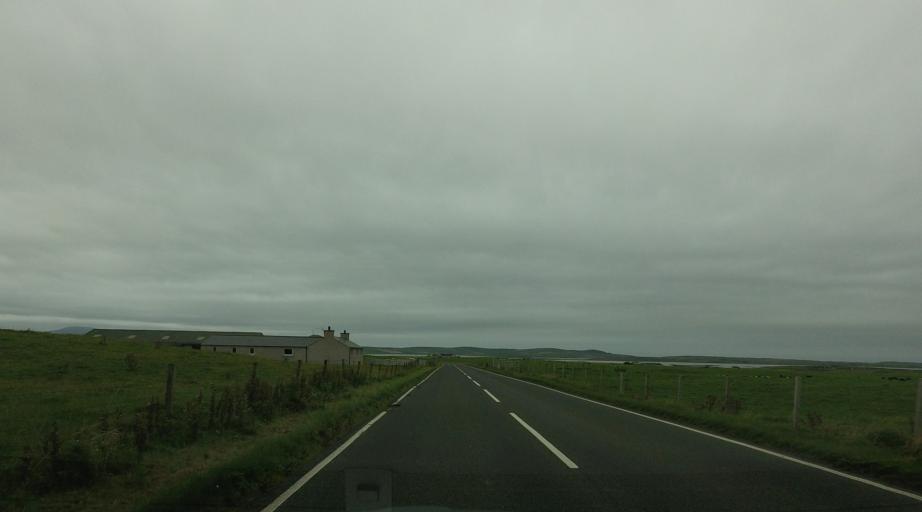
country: GB
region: Scotland
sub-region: Orkney Islands
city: Stromness
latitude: 59.0038
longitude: -3.1642
